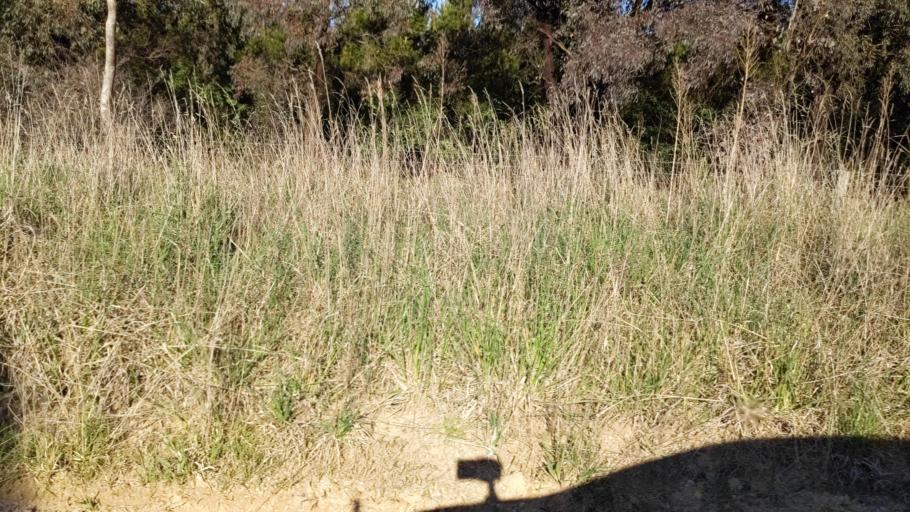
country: AU
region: New South Wales
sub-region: Blayney
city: Millthorpe
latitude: -33.4011
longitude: 149.3084
